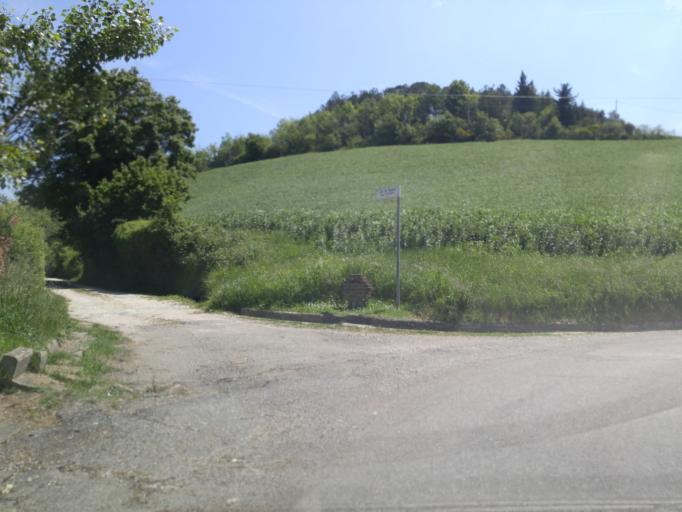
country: IT
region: The Marches
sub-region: Provincia di Pesaro e Urbino
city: Fermignano
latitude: 43.7014
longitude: 12.6445
